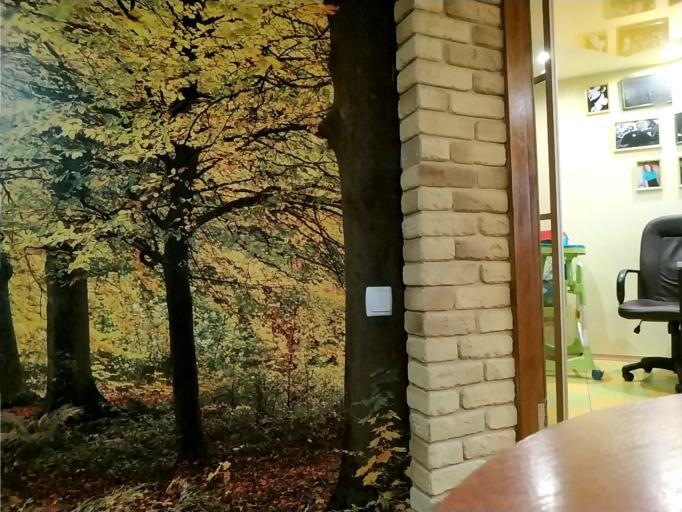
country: RU
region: Tverskaya
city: Staraya Toropa
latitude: 56.3405
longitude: 31.8523
